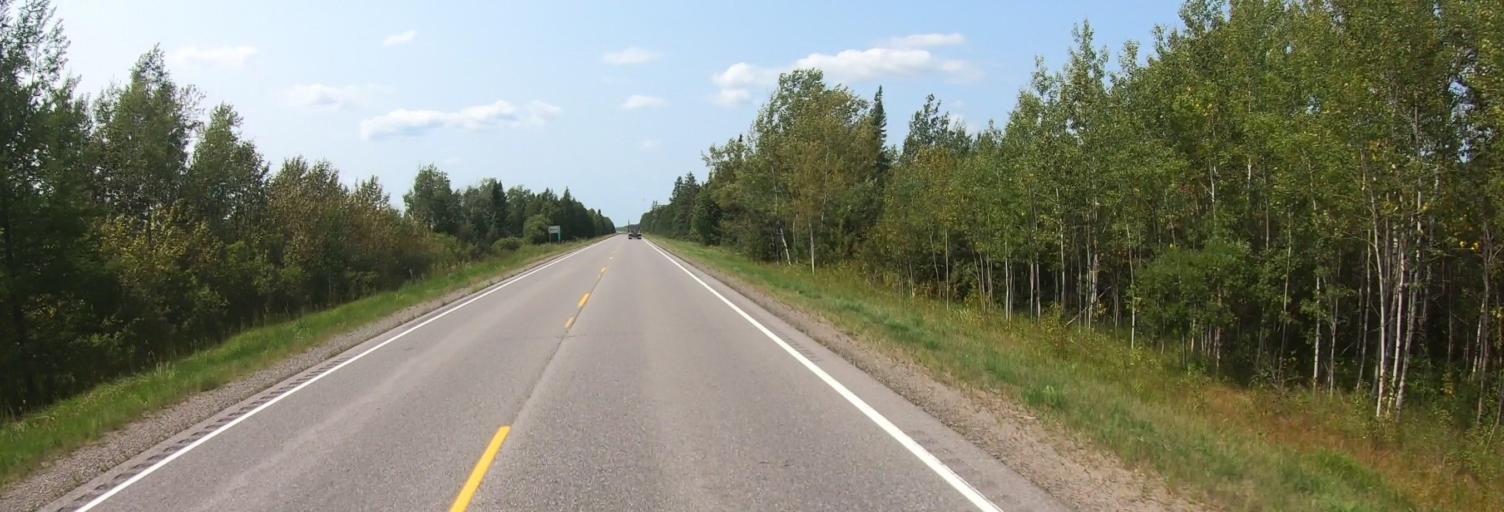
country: US
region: Minnesota
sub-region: Koochiching County
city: International Falls
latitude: 48.6286
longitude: -93.9833
